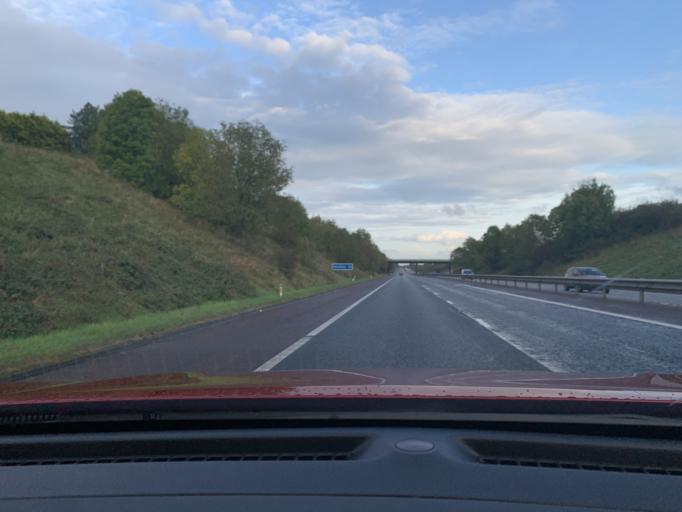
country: GB
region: Northern Ireland
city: Coalisland
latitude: 54.4950
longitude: -6.6900
